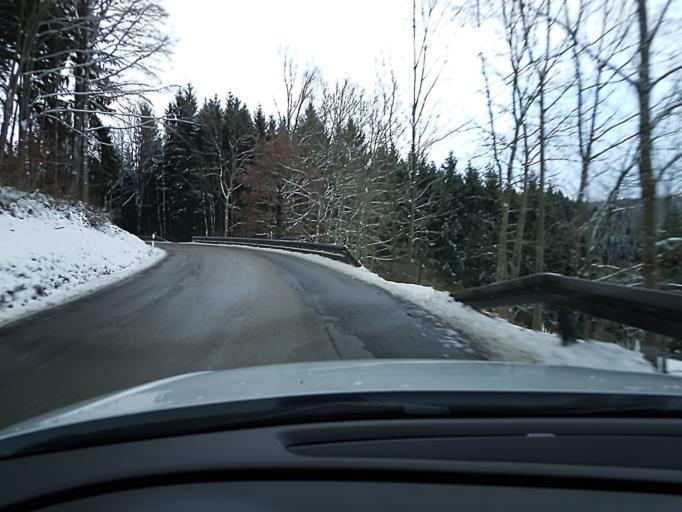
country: DE
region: Baden-Wuerttemberg
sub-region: Regierungsbezirk Stuttgart
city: Kaisersbach
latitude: 48.9553
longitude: 9.6613
